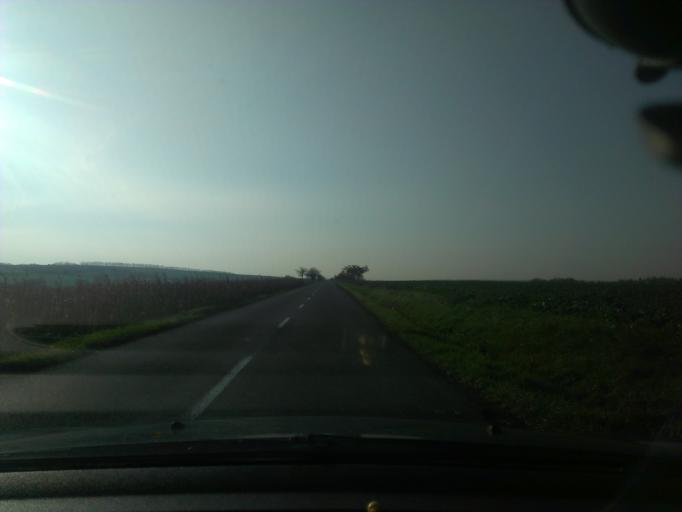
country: SK
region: Trnavsky
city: Hlohovec
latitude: 48.4865
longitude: 17.9892
